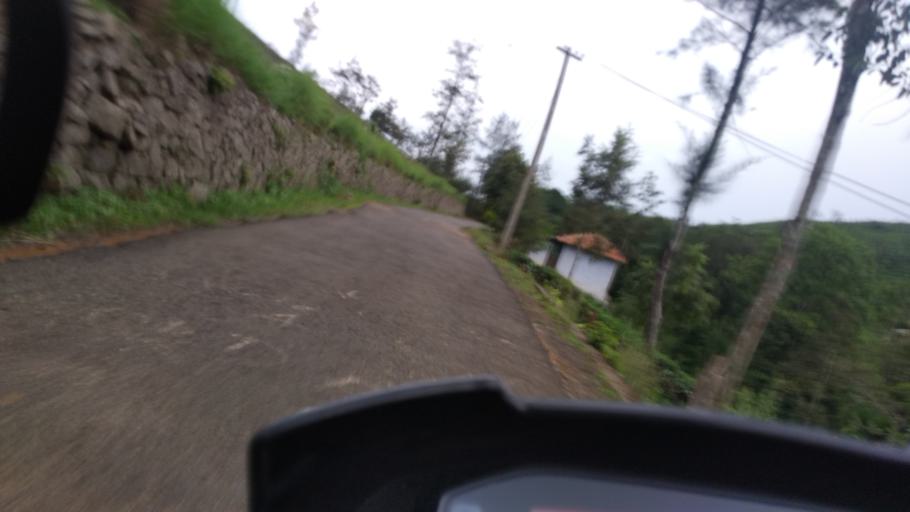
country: IN
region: Tamil Nadu
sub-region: Theni
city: Gudalur
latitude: 9.5419
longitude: 77.0456
